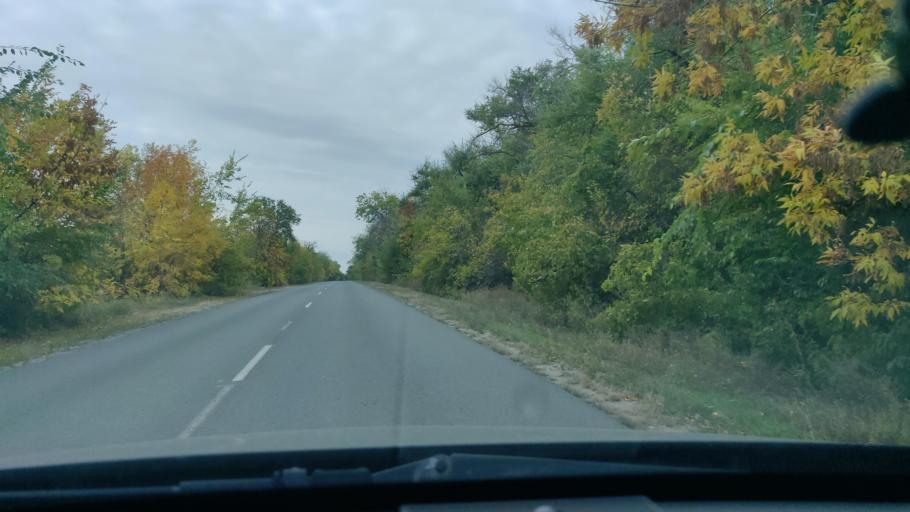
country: RU
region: Rostov
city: Ust'-Donetskiy
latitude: 47.6505
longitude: 40.8904
